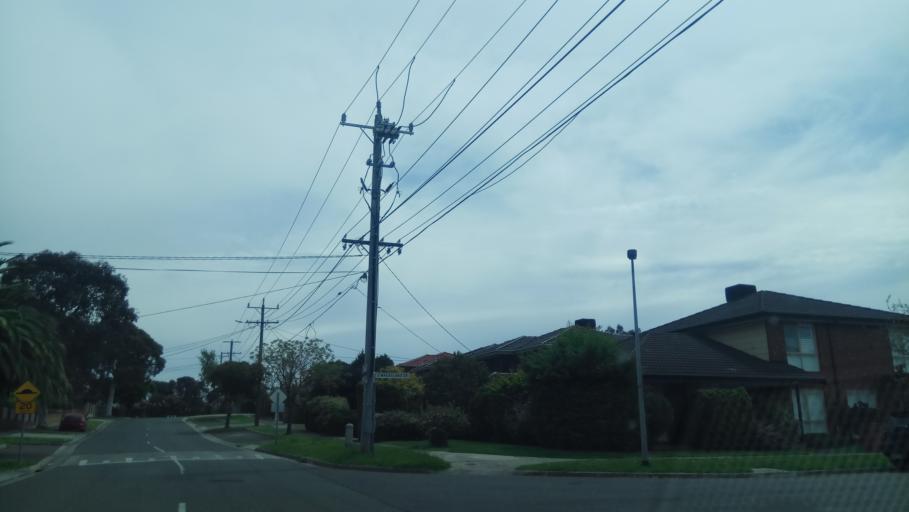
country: AU
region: Victoria
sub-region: Kingston
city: Dingley Village
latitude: -37.9684
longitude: 145.1267
